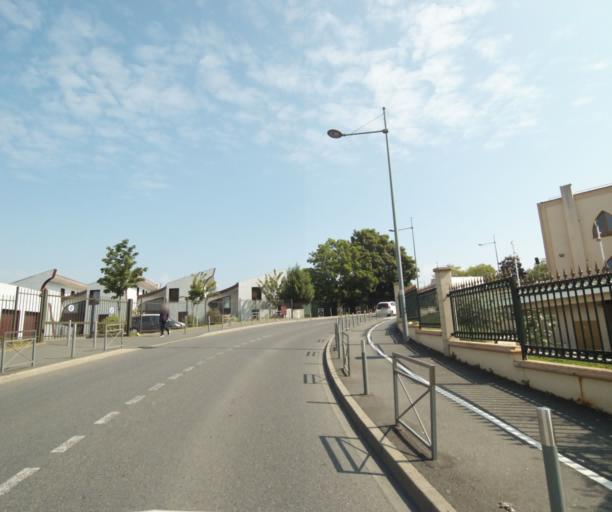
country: FR
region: Ile-de-France
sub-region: Departement du Val-d'Oise
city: Argenteuil
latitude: 48.9521
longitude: 2.2342
